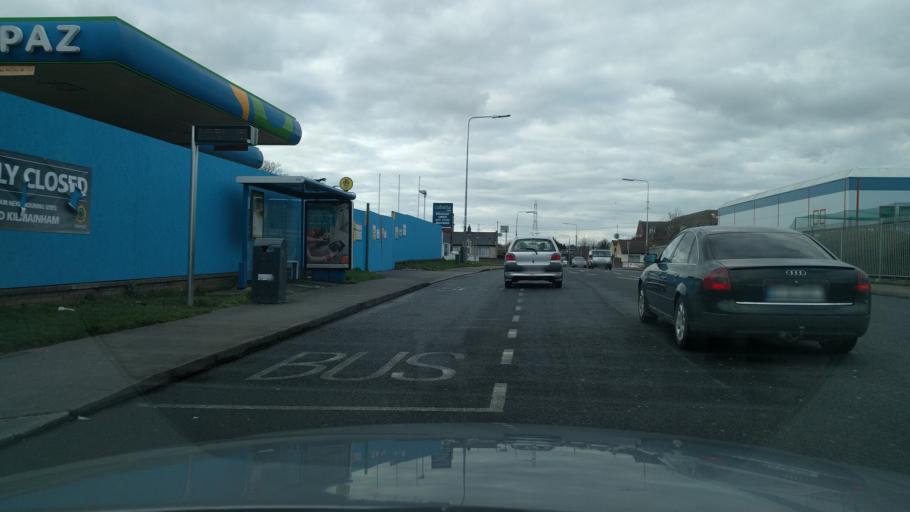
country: IE
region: Leinster
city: Crumlin
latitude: 53.3278
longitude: -6.3436
